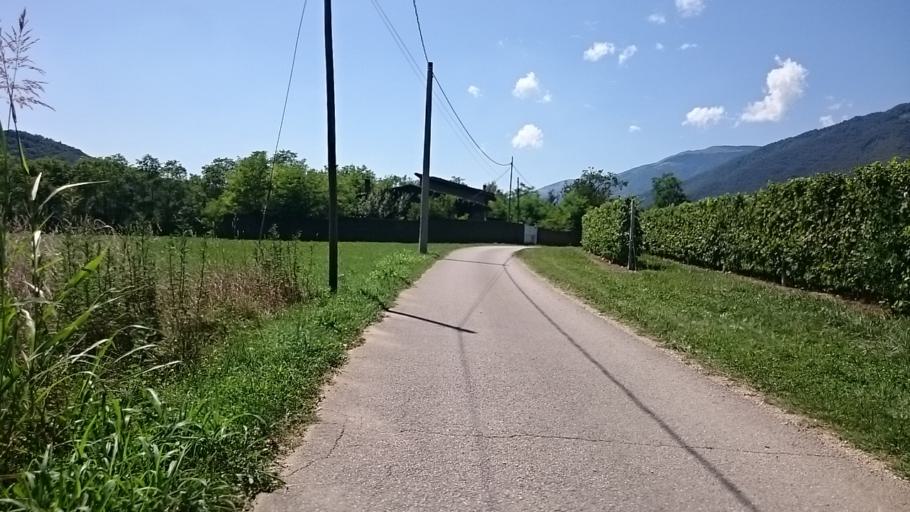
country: IT
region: Veneto
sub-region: Provincia di Treviso
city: Cison di Valmarino
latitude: 45.9621
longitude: 12.1490
